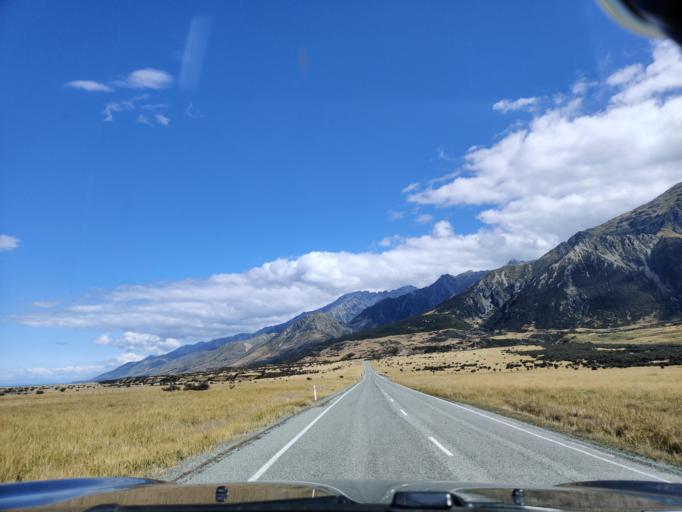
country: NZ
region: Canterbury
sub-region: Timaru District
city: Pleasant Point
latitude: -43.7910
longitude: 170.1191
